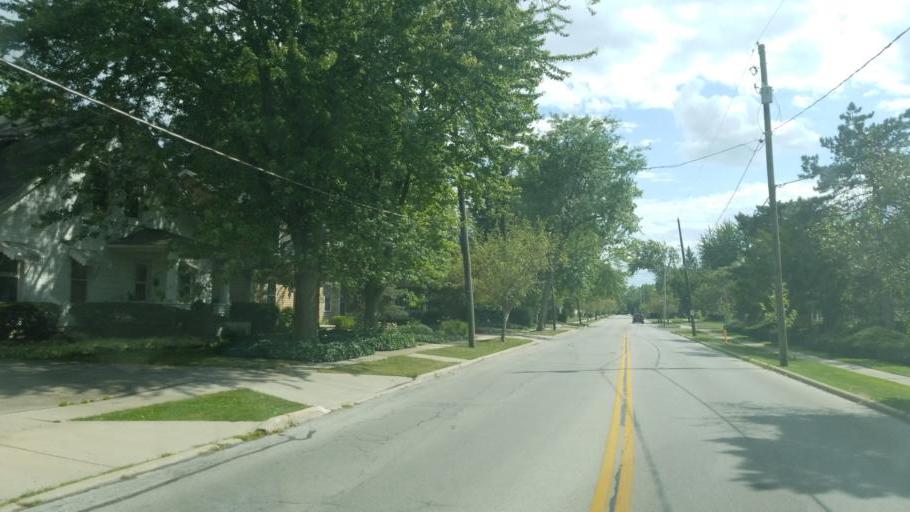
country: US
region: Ohio
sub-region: Lucas County
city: Maumee
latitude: 41.5673
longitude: -83.6454
